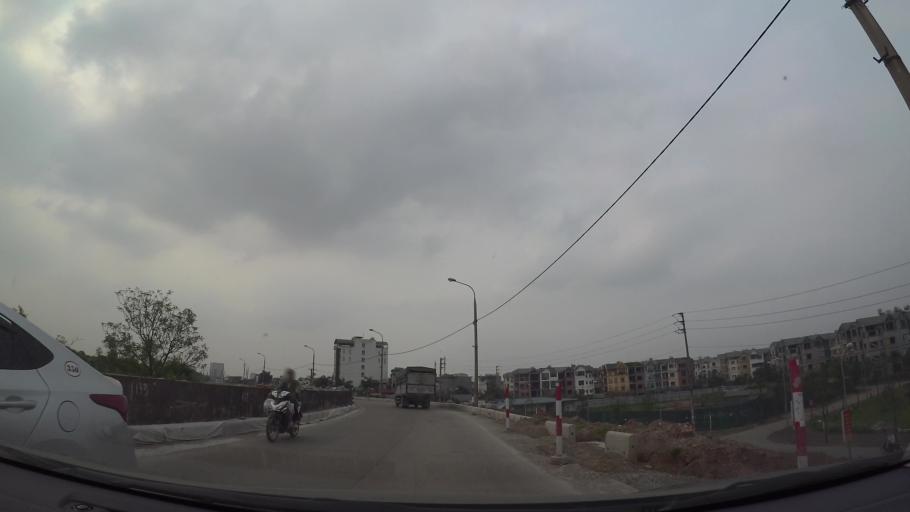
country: VN
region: Ha Noi
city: Trau Quy
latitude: 21.0180
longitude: 105.9042
